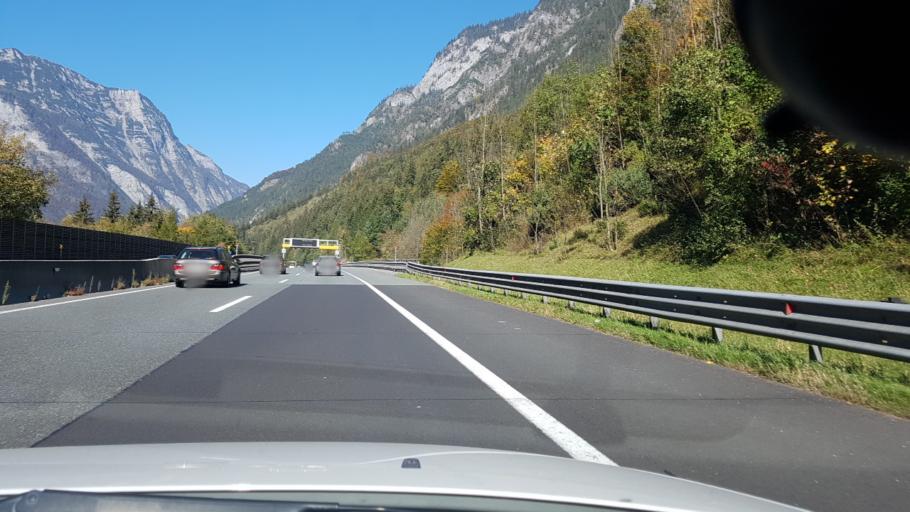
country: AT
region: Salzburg
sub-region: Politischer Bezirk Sankt Johann im Pongau
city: Werfen
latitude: 47.4967
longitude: 13.1807
